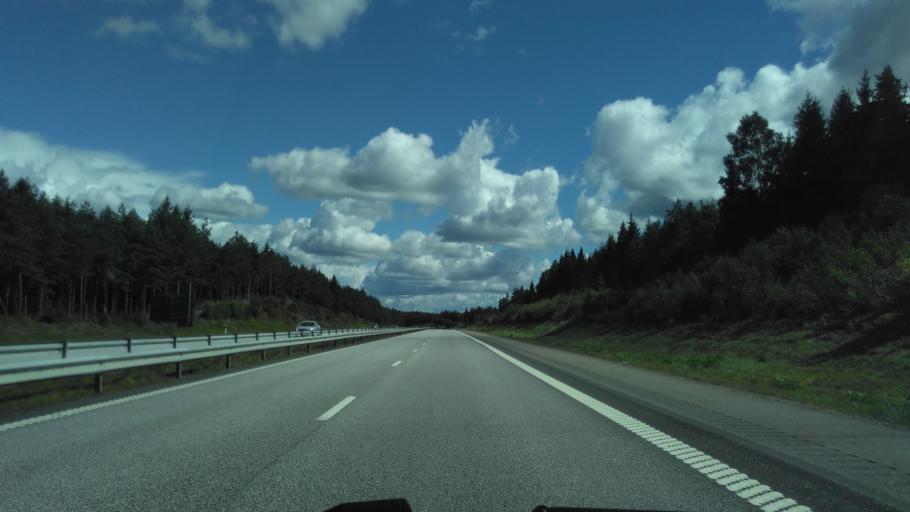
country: SE
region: Vaestra Goetaland
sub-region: Harryda Kommun
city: Hindas
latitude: 57.6701
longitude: 12.3748
